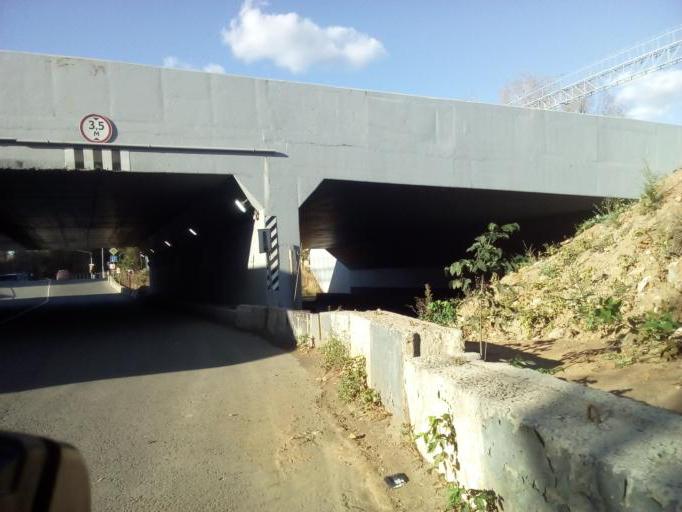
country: RU
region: Moscow
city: Zapadnoye Degunino
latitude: 55.8450
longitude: 37.5422
